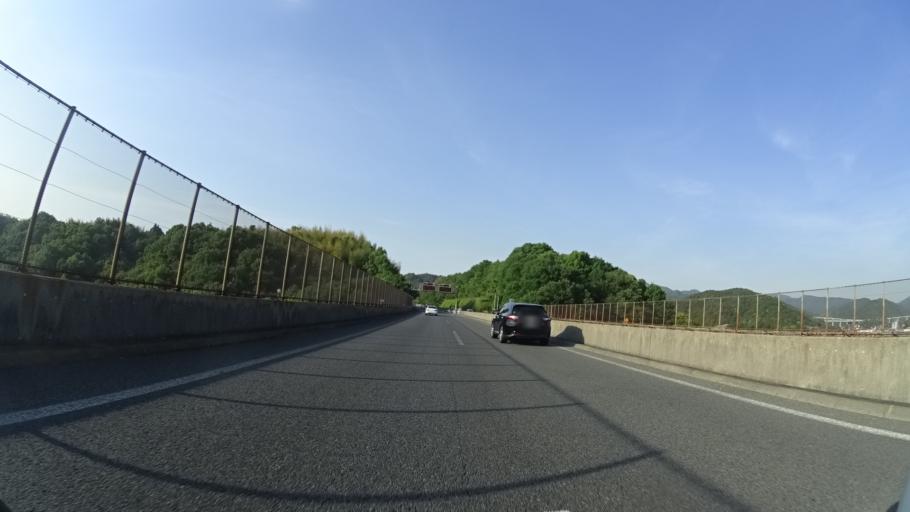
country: JP
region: Ehime
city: Kawanoecho
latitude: 33.9915
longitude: 133.5939
